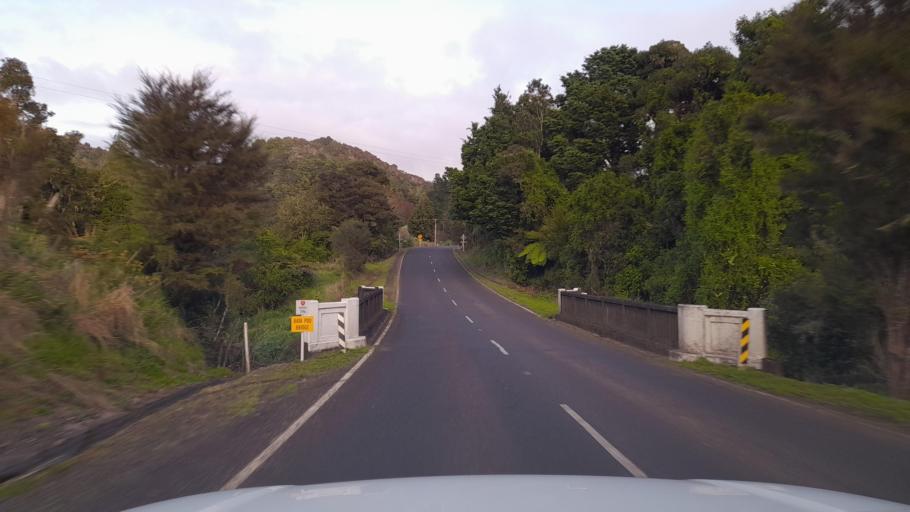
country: NZ
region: Northland
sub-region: Kaipara District
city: Dargaville
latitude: -35.6405
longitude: 173.8551
